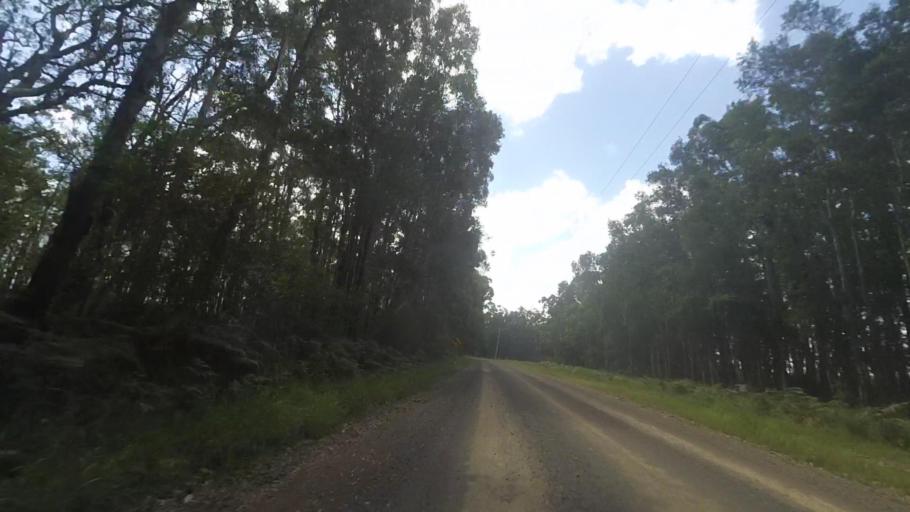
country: AU
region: New South Wales
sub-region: Great Lakes
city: Bulahdelah
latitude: -32.5027
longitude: 152.2898
